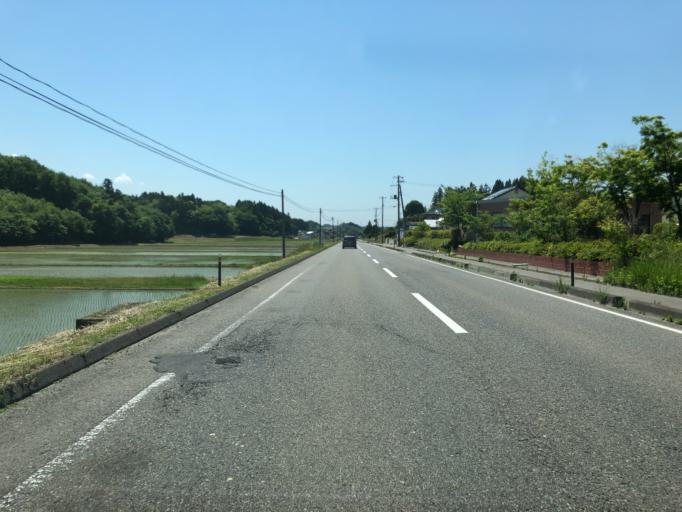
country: JP
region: Fukushima
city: Motomiya
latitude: 37.5069
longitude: 140.4580
